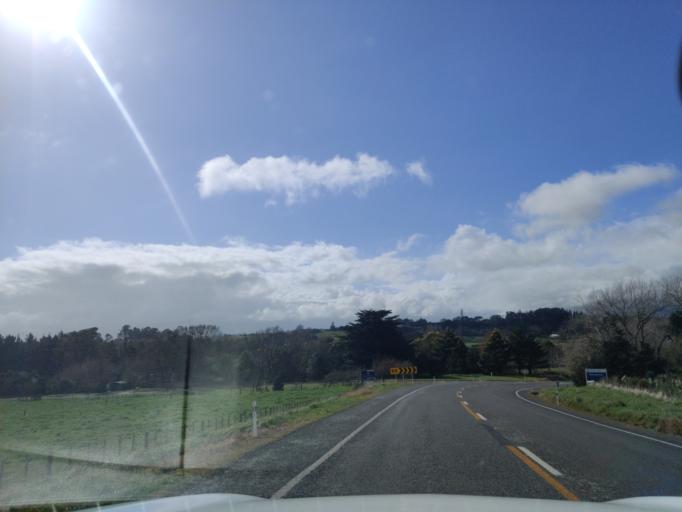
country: NZ
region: Manawatu-Wanganui
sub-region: Palmerston North City
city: Palmerston North
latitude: -40.3953
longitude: 175.6280
